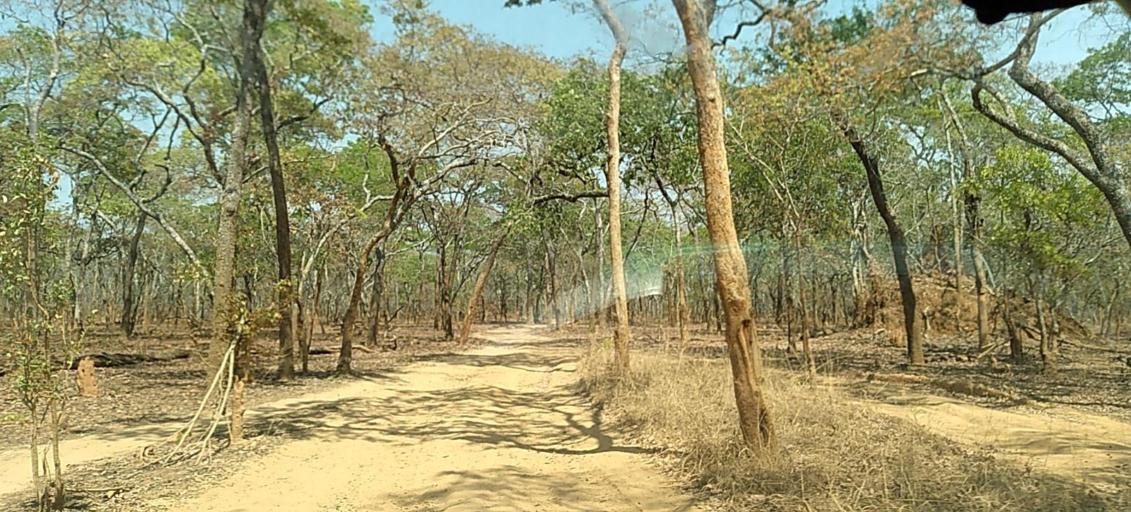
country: ZM
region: North-Western
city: Kasempa
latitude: -13.3924
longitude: 25.6176
